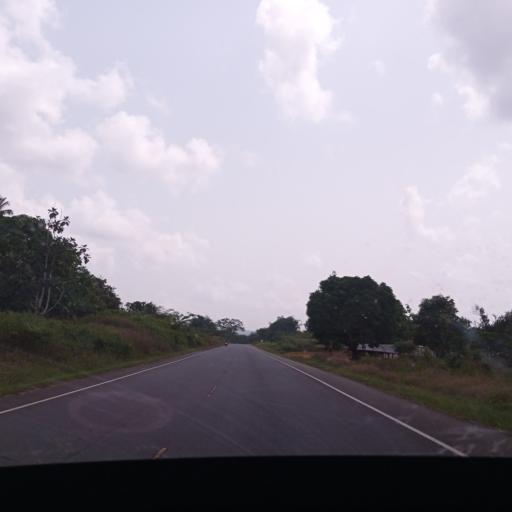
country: LR
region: Margibi
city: Kakata
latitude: 6.2441
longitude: -10.2905
